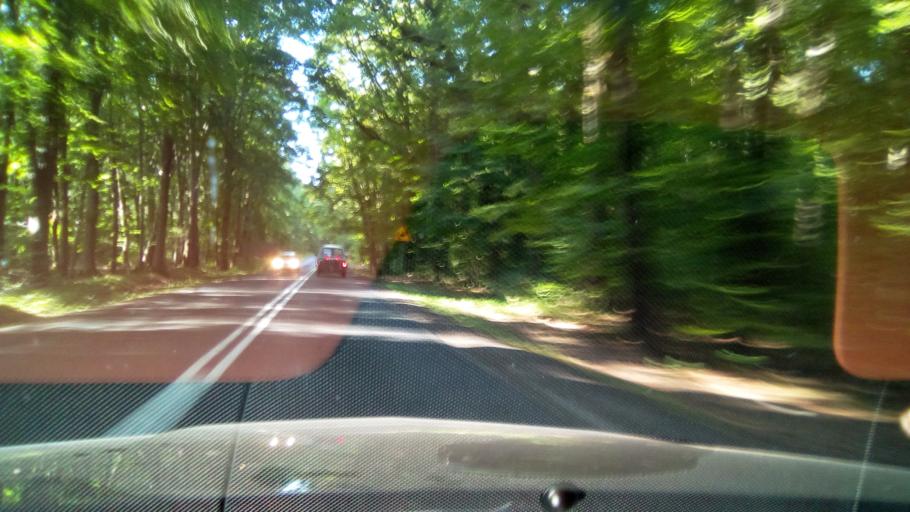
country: PL
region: West Pomeranian Voivodeship
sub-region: Powiat kamienski
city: Golczewo
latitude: 53.8081
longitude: 15.0090
